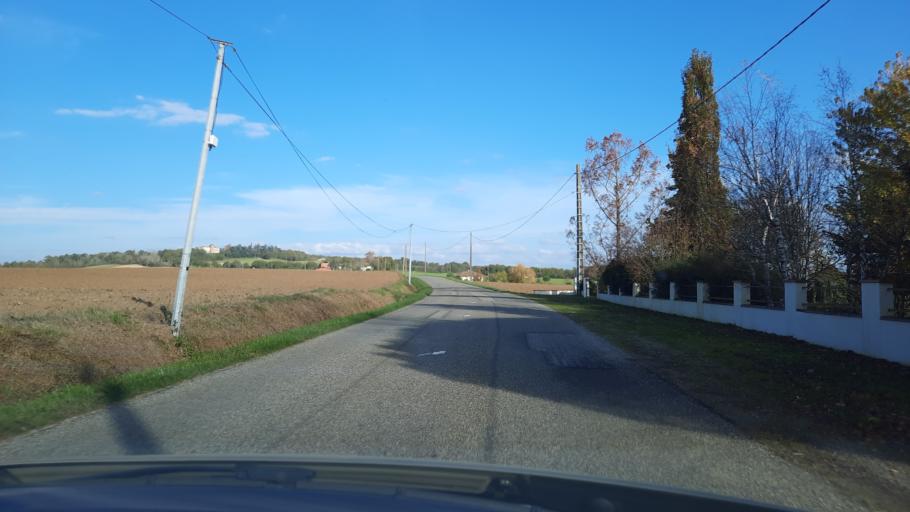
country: FR
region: Midi-Pyrenees
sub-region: Departement du Tarn-et-Garonne
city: Lafrancaise
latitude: 44.1685
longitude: 1.2720
